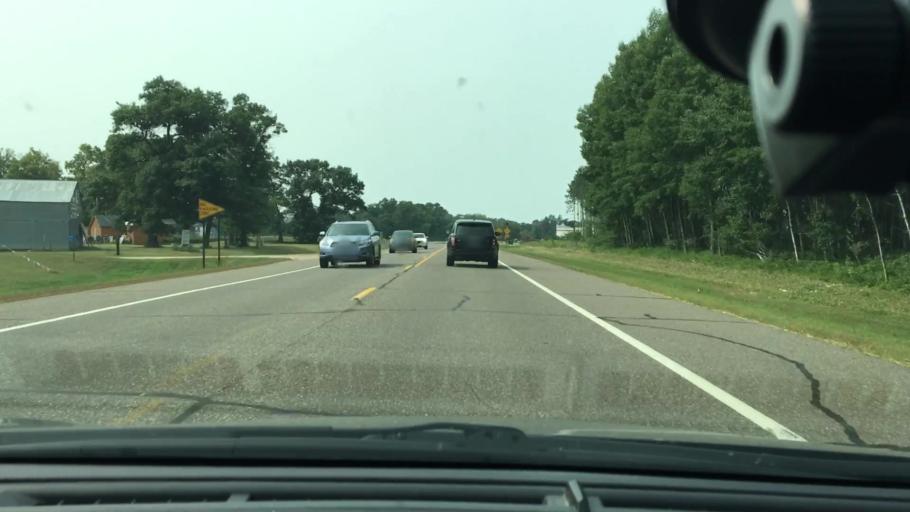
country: US
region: Minnesota
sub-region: Crow Wing County
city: Breezy Point
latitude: 46.4902
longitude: -94.1536
